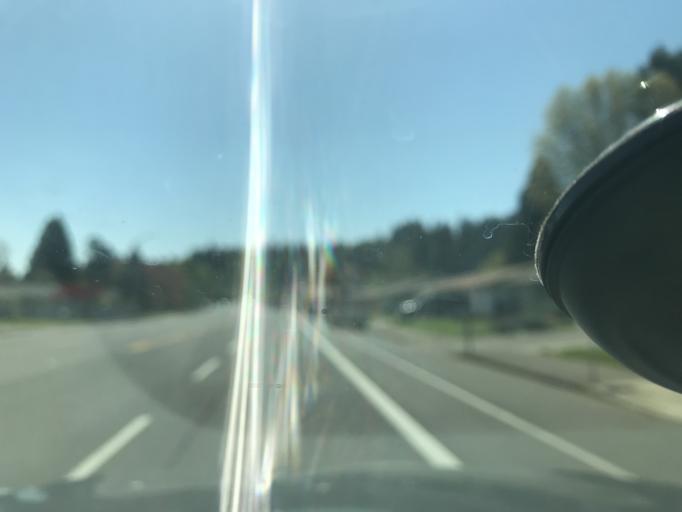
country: US
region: Oregon
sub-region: Clackamas County
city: Happy Valley
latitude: 45.4984
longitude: -122.4970
